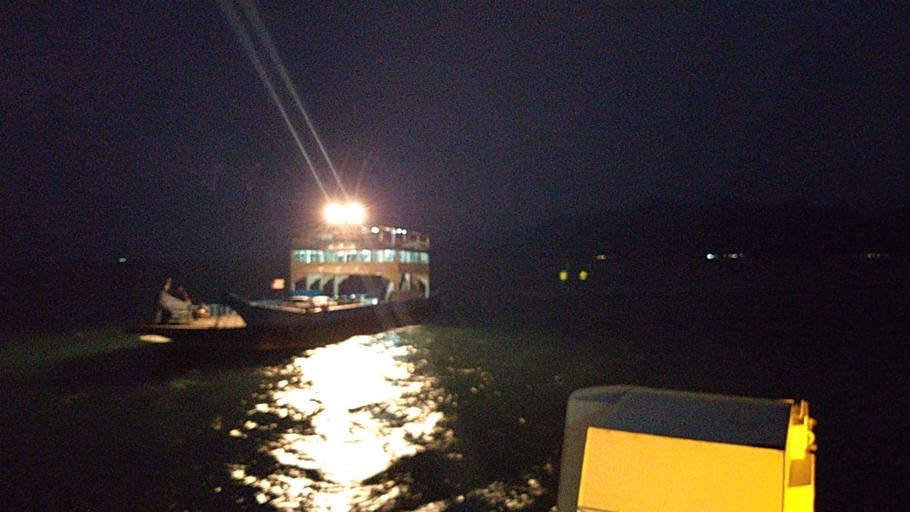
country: TH
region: Trat
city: Laem Ngop
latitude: 12.1844
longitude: 102.3017
